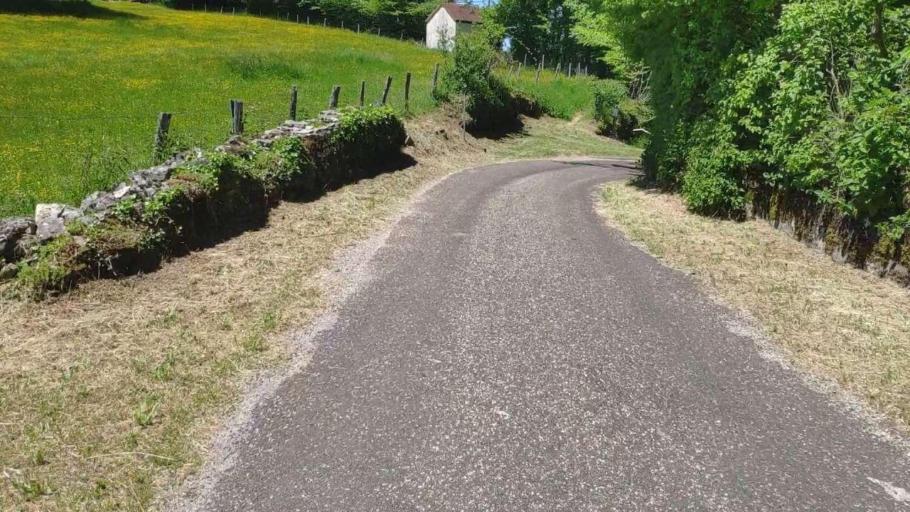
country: FR
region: Franche-Comte
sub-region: Departement du Jura
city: Poligny
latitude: 46.7443
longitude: 5.6726
